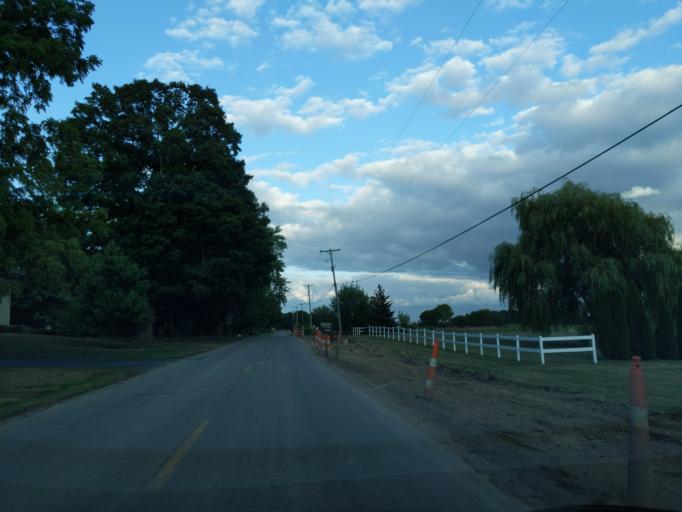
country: US
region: Michigan
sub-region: Ingham County
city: Holt
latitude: 42.5967
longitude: -84.5415
